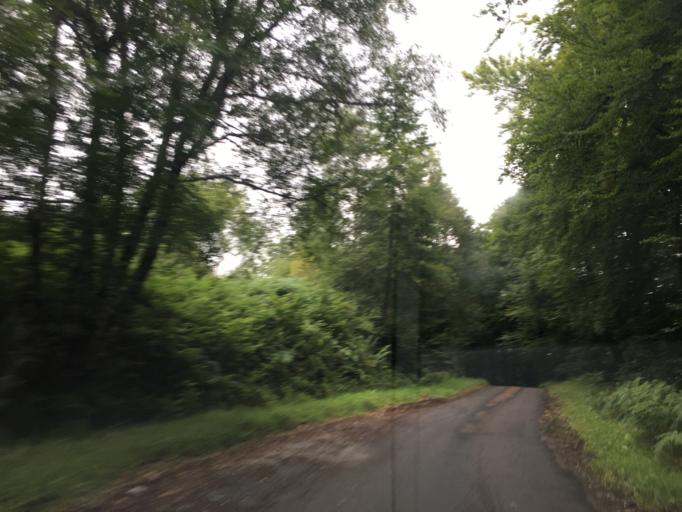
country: GB
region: Scotland
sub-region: Argyll and Bute
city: Oban
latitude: 56.2763
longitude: -5.2829
